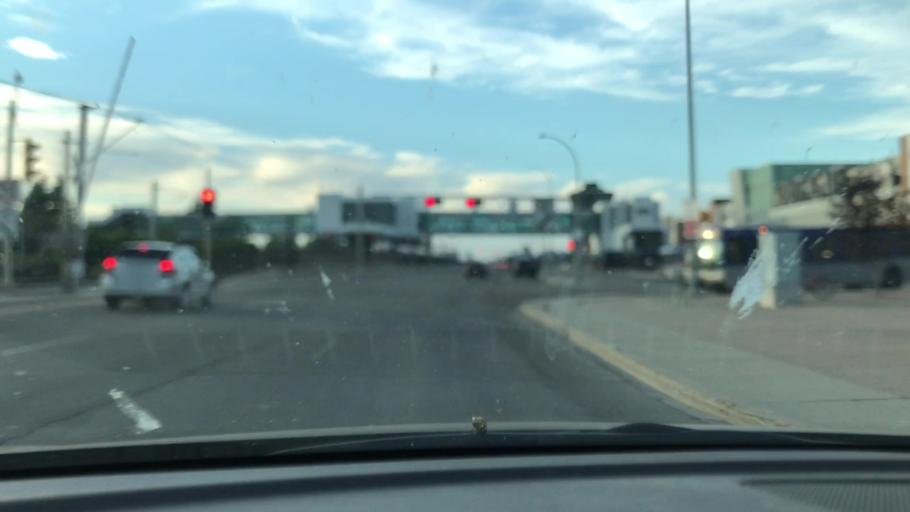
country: CA
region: Alberta
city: Edmonton
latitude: 53.4844
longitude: -113.5153
